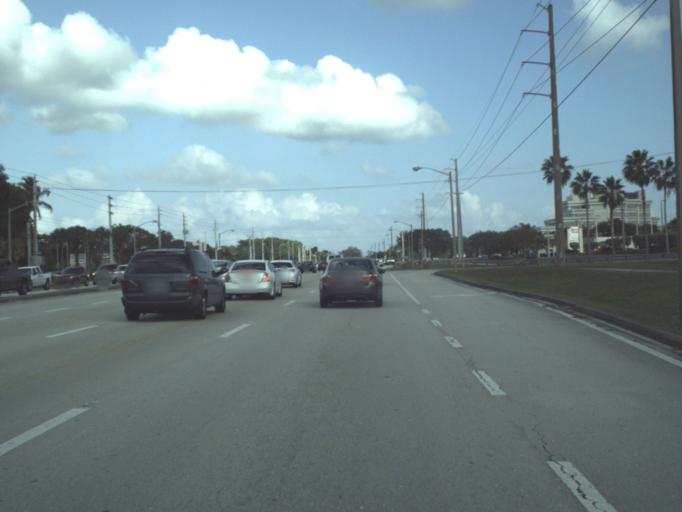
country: US
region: Florida
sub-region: Palm Beach County
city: Boca Del Mar
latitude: 26.3502
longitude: -80.1593
